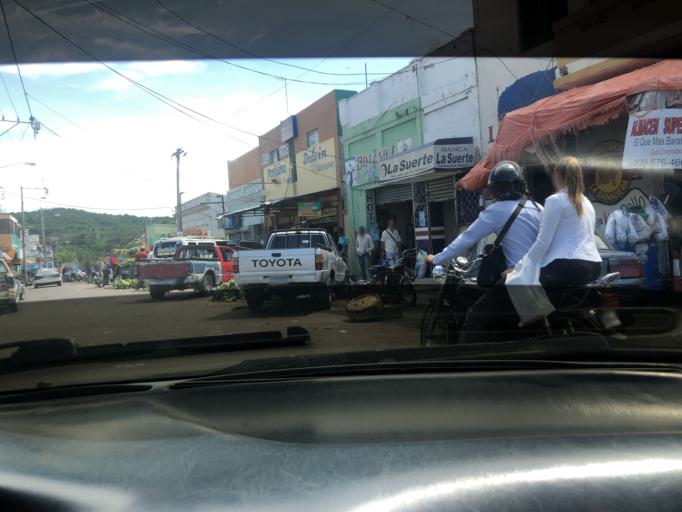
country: DO
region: Santiago
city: Santiago de los Caballeros
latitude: 19.4511
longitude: -70.7102
